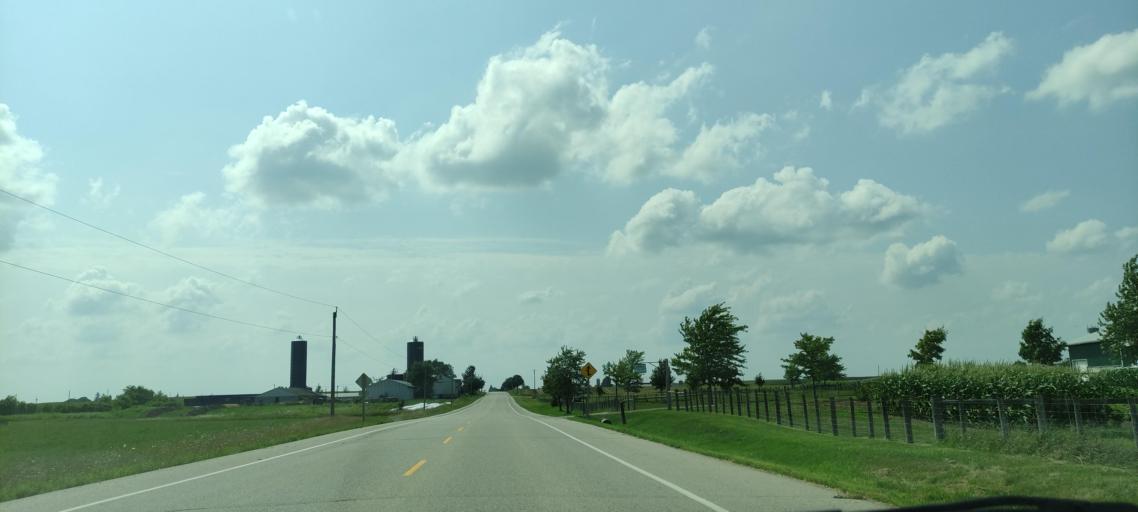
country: CA
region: Ontario
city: Waterloo
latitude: 43.4732
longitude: -80.7185
